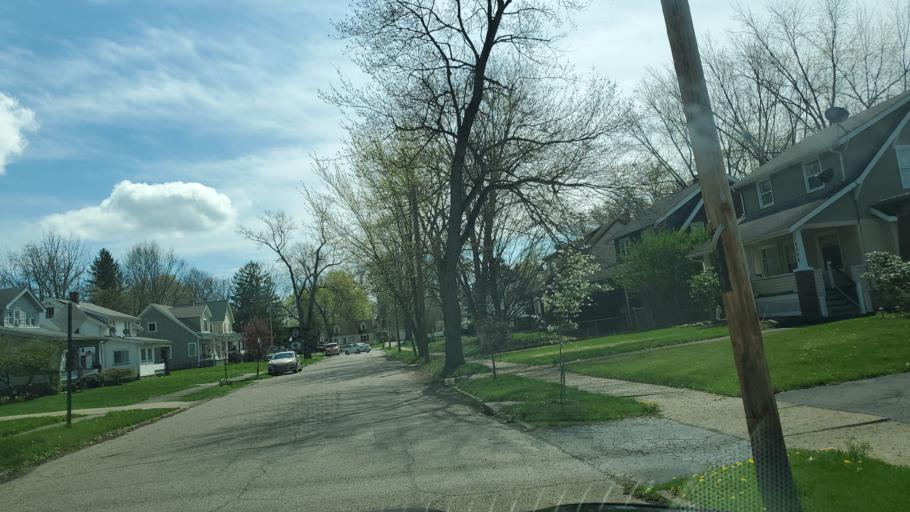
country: US
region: Ohio
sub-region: Mahoning County
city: Boardman
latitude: 41.0561
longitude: -80.6591
